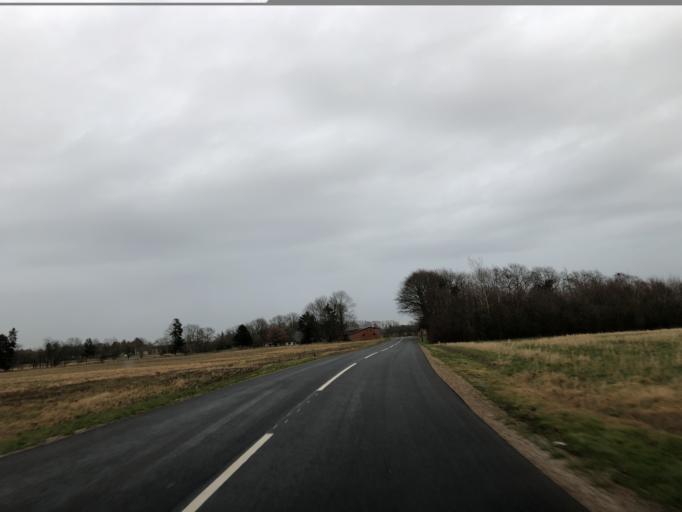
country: DK
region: Central Jutland
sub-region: Holstebro Kommune
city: Vinderup
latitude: 56.3810
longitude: 8.8399
